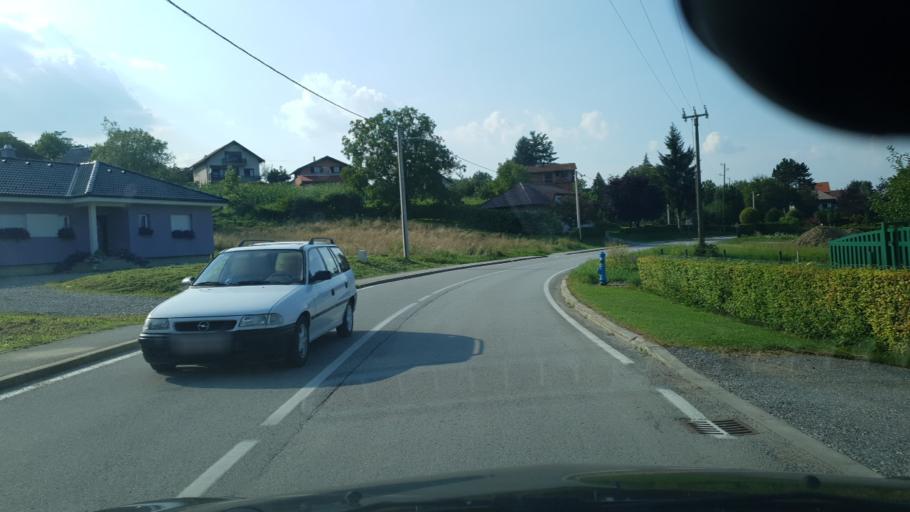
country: HR
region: Krapinsko-Zagorska
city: Oroslavje
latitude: 45.9678
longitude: 15.9162
